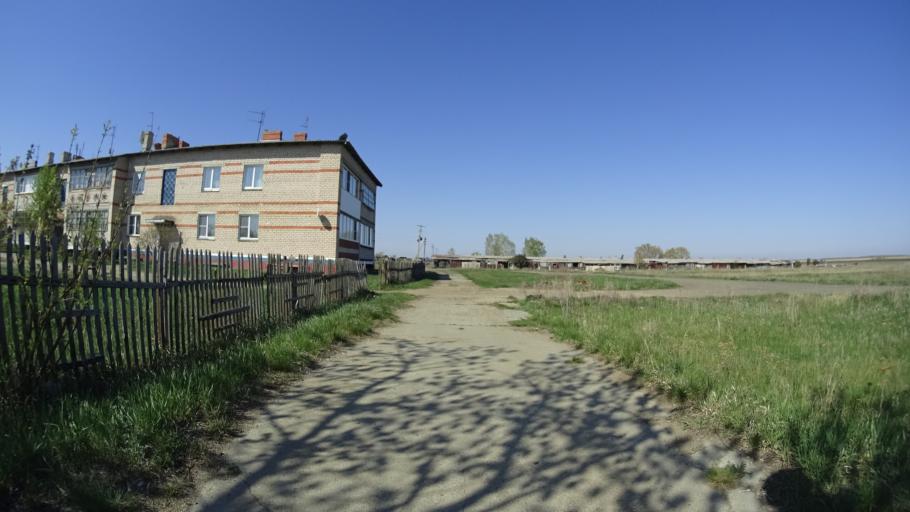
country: RU
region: Chelyabinsk
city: Troitsk
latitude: 54.1907
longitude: 61.5034
